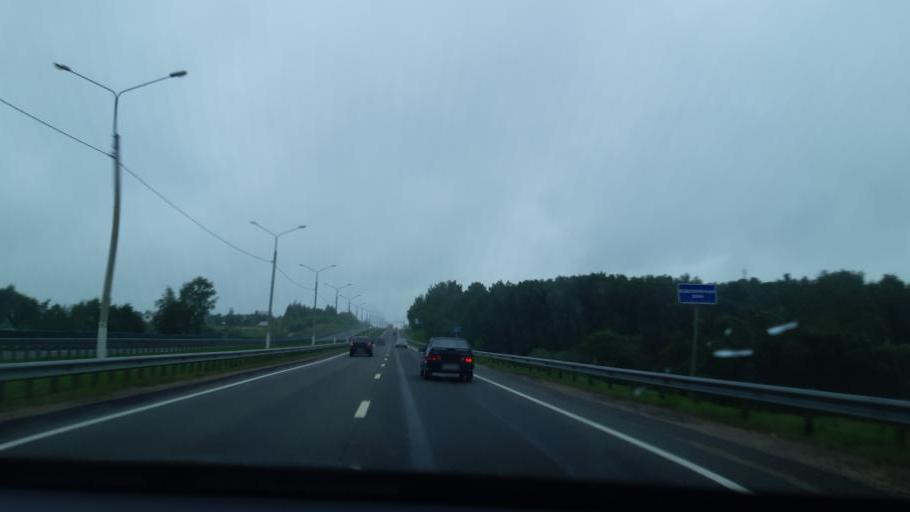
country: RU
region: Smolensk
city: Talashkino
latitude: 54.6757
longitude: 32.1453
